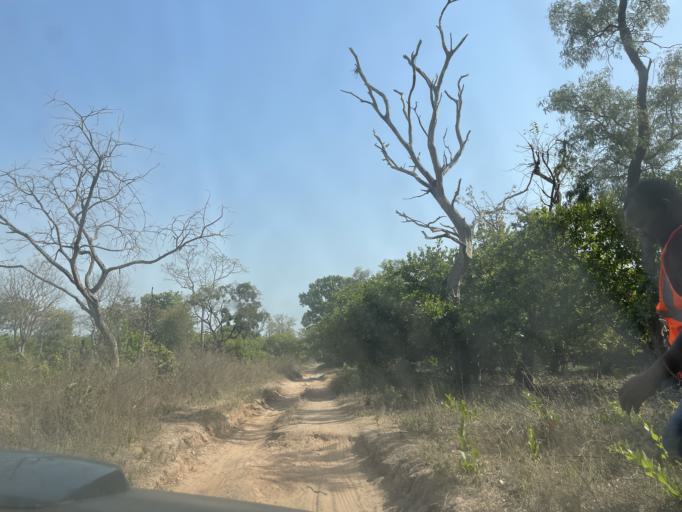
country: GW
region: Oio
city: Bissora
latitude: 12.3662
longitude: -15.7044
